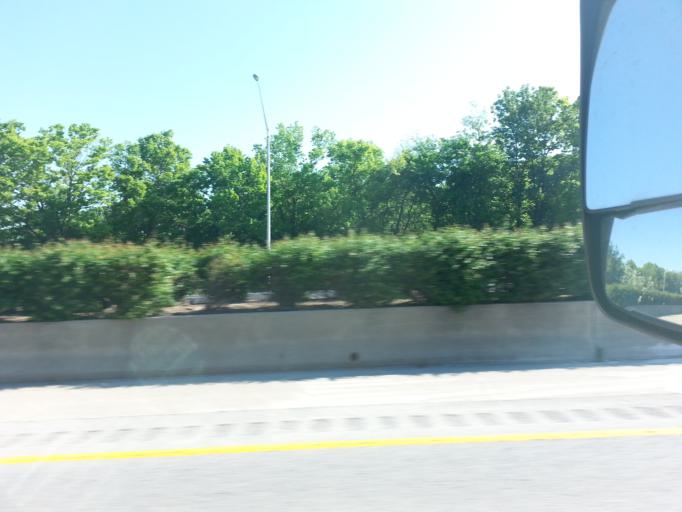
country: US
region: Kentucky
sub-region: Jefferson County
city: Hurstbourne Acres
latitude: 38.2294
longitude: -85.5982
